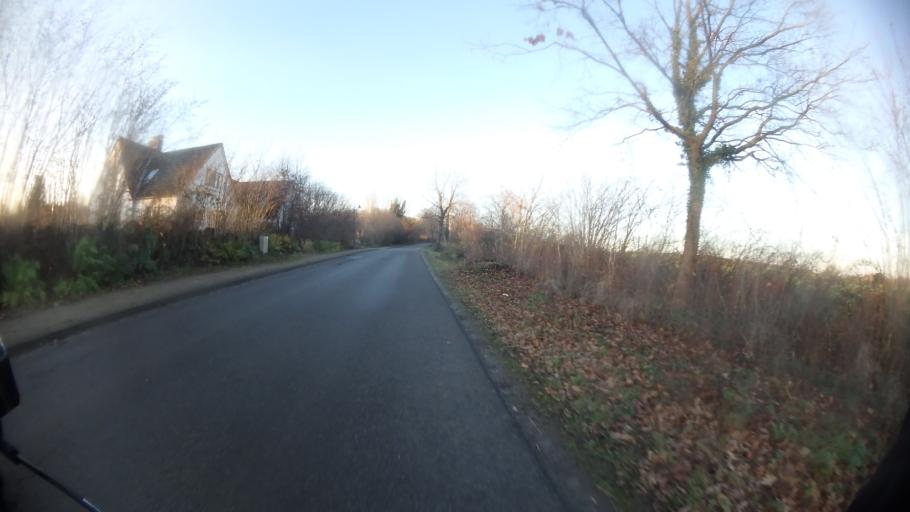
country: DE
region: Schleswig-Holstein
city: Scharbeutz
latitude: 54.0165
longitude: 10.7020
